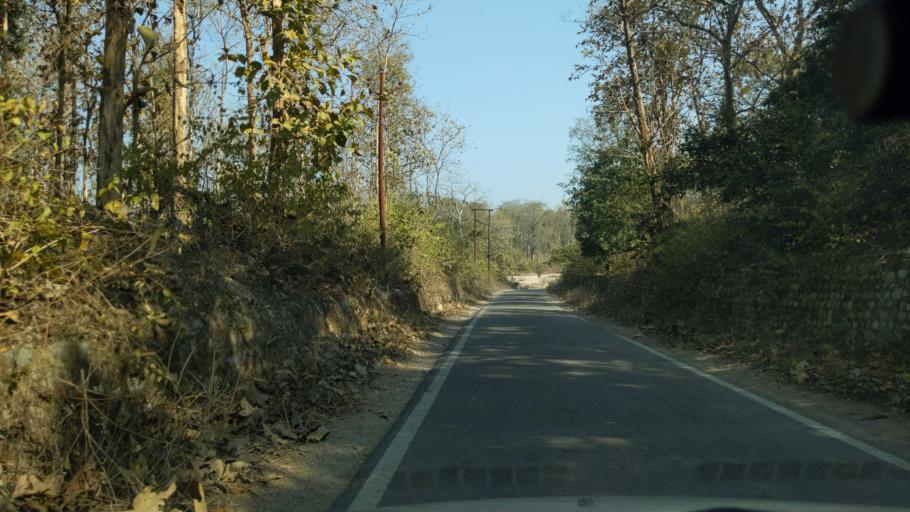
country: IN
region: Uttarakhand
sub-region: Naini Tal
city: Ramnagar
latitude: 29.4063
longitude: 79.1376
